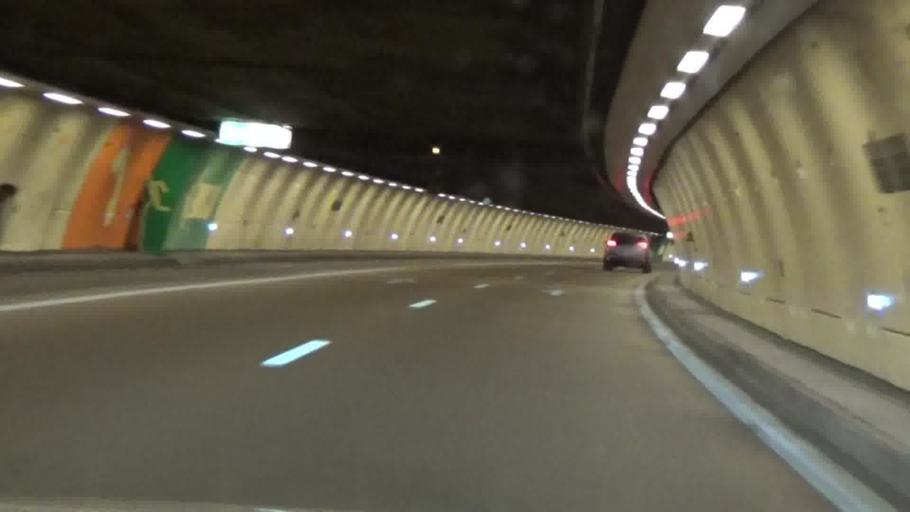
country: FR
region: Ile-de-France
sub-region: Departement des Yvelines
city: La Celle-Saint-Cloud
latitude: 48.8383
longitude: 2.1441
